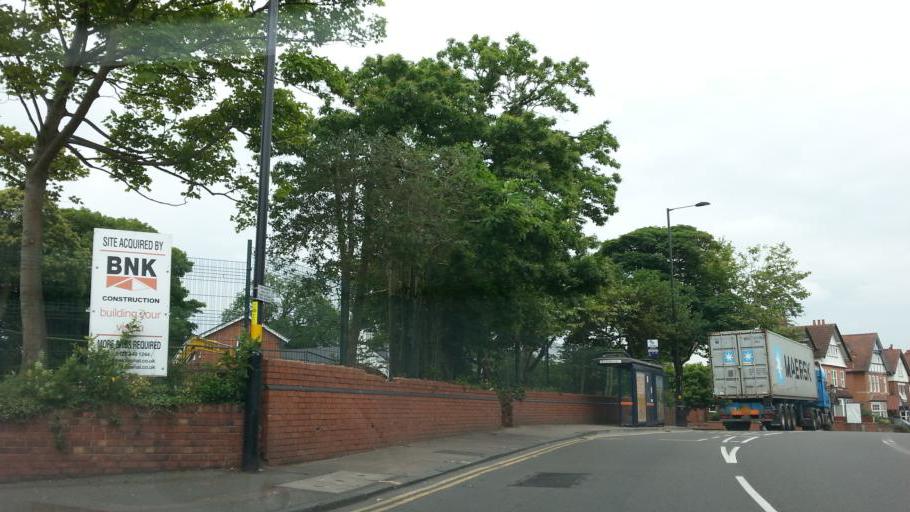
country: GB
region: England
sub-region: City and Borough of Birmingham
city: Birmingham
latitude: 52.4421
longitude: -1.8924
